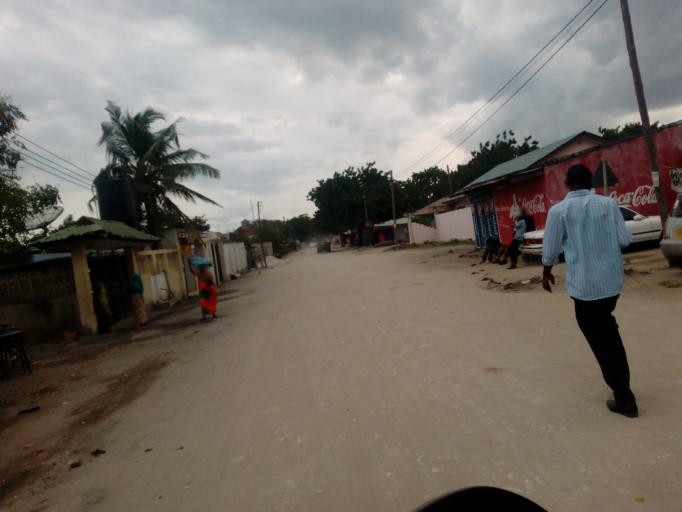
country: TZ
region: Dar es Salaam
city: Dar es Salaam
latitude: -6.8427
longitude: 39.2762
